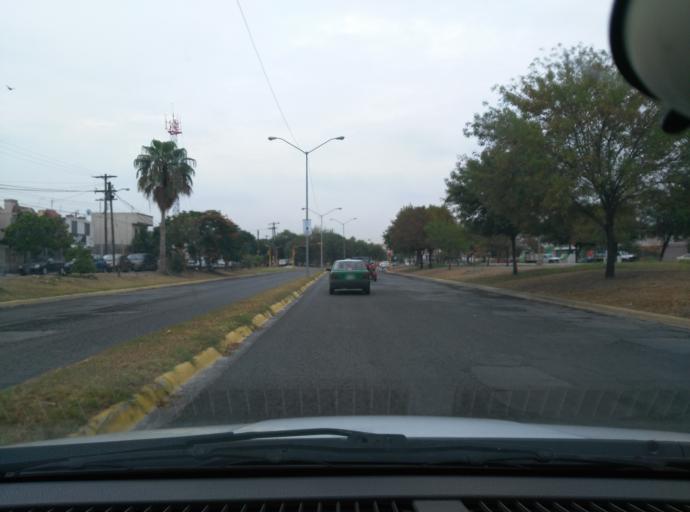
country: MX
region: Nuevo Leon
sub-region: Apodaca
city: Fraccionamiento Cosmopolis Octavo Sector
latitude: 25.7706
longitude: -100.2502
